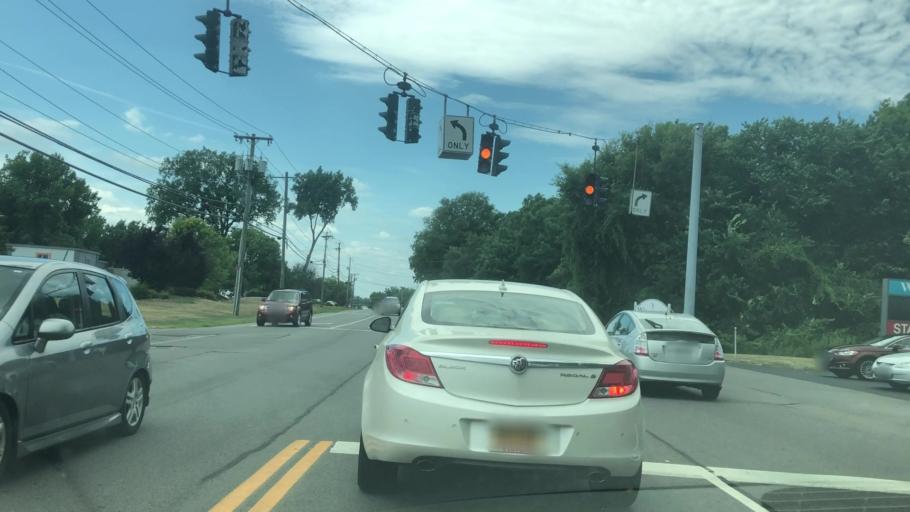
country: US
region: New York
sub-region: Monroe County
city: Webster
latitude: 43.2079
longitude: -77.4646
